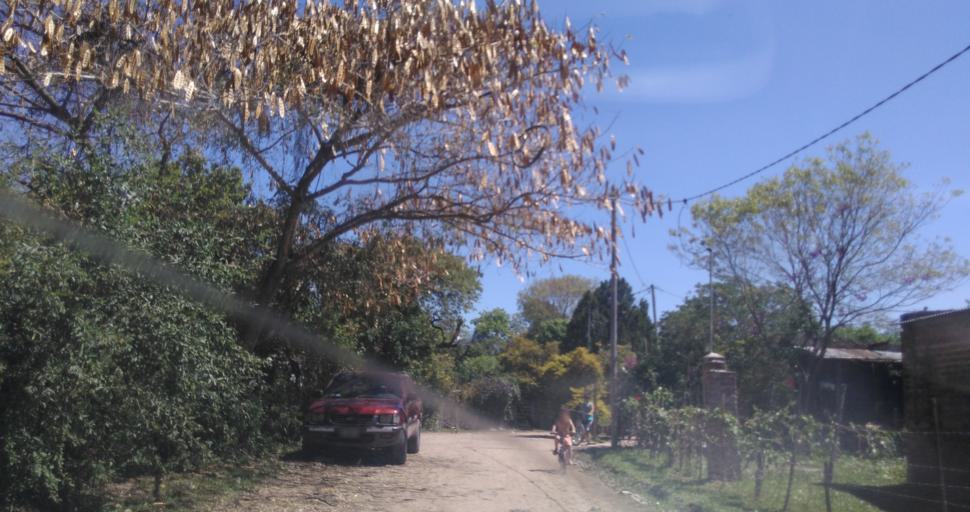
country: AR
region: Chaco
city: Resistencia
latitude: -27.4226
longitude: -58.9815
